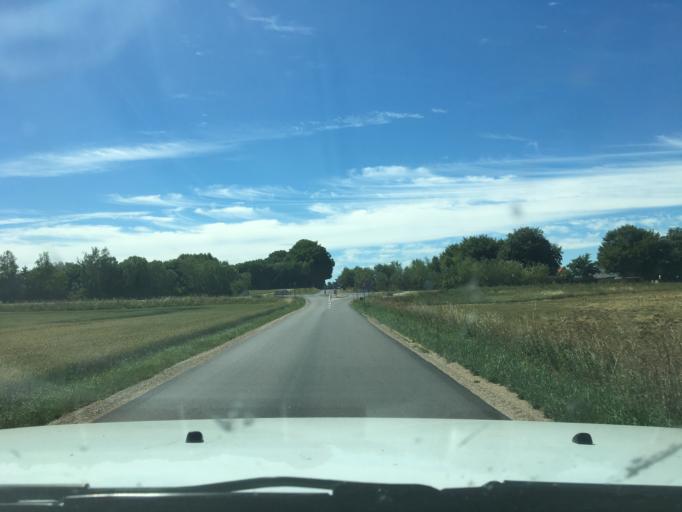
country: DK
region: Central Jutland
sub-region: Syddjurs Kommune
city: Ryomgard
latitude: 56.4310
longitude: 10.5677
